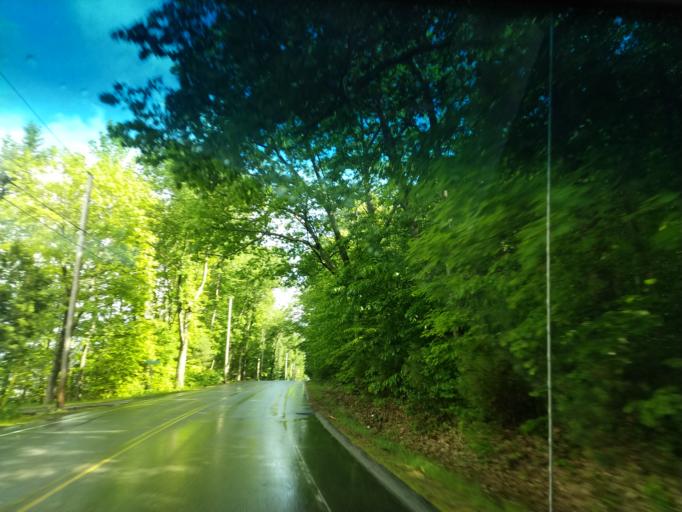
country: US
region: Maine
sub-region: Cumberland County
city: Cumberland Center
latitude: 43.7610
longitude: -70.3184
